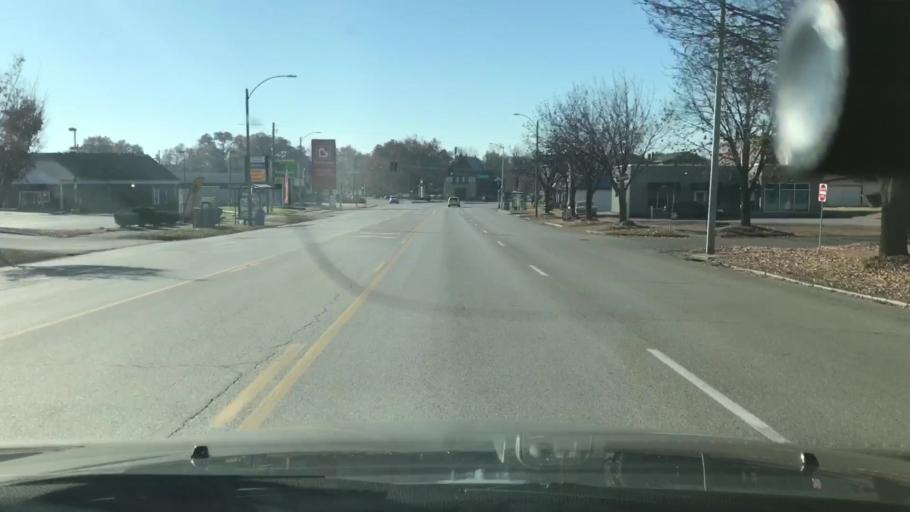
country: US
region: Missouri
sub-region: Saint Louis County
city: Lemay
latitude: 38.5863
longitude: -90.2765
